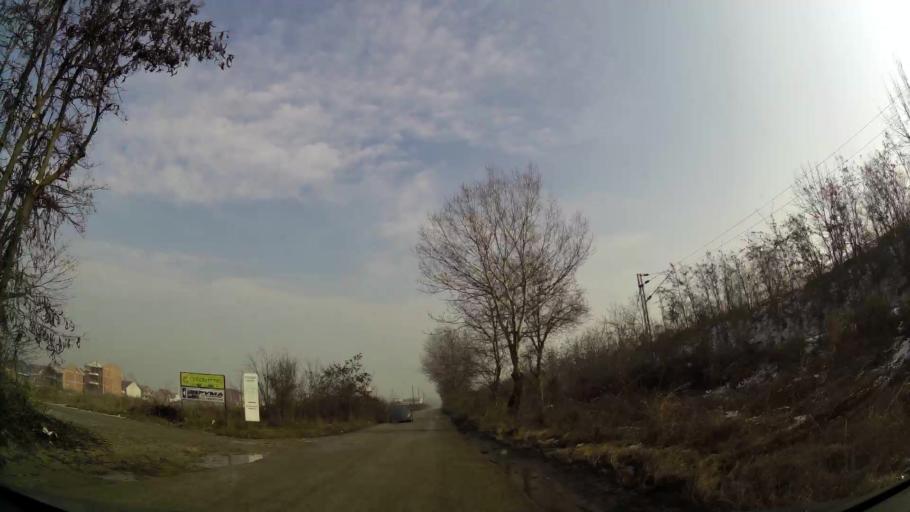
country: MK
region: Kisela Voda
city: Kisela Voda
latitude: 41.9913
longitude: 21.5135
